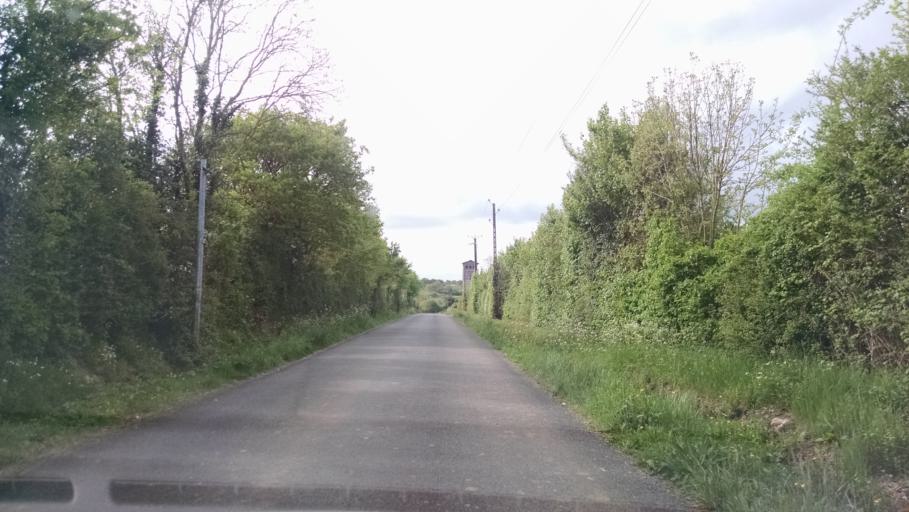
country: FR
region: Pays de la Loire
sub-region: Departement de la Vendee
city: Saint-Hilaire-de-Loulay
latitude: 46.9892
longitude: -1.3477
